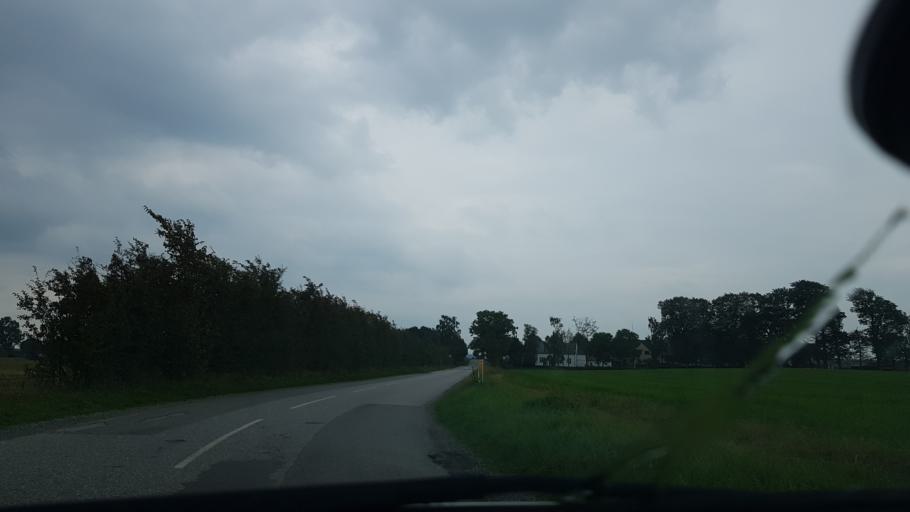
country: DK
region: South Denmark
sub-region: Kolding Kommune
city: Lunderskov
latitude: 55.5346
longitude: 9.3404
